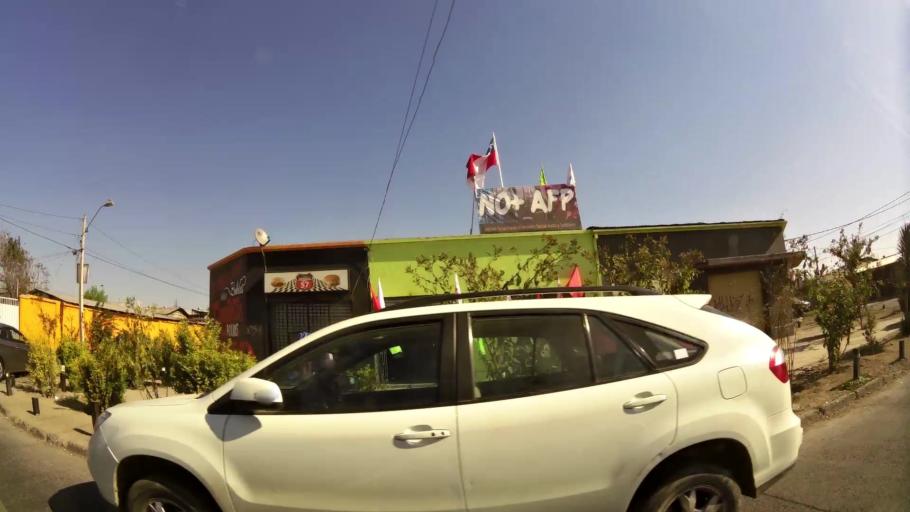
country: CL
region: Santiago Metropolitan
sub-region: Provincia de Santiago
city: Santiago
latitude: -33.5160
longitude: -70.6872
